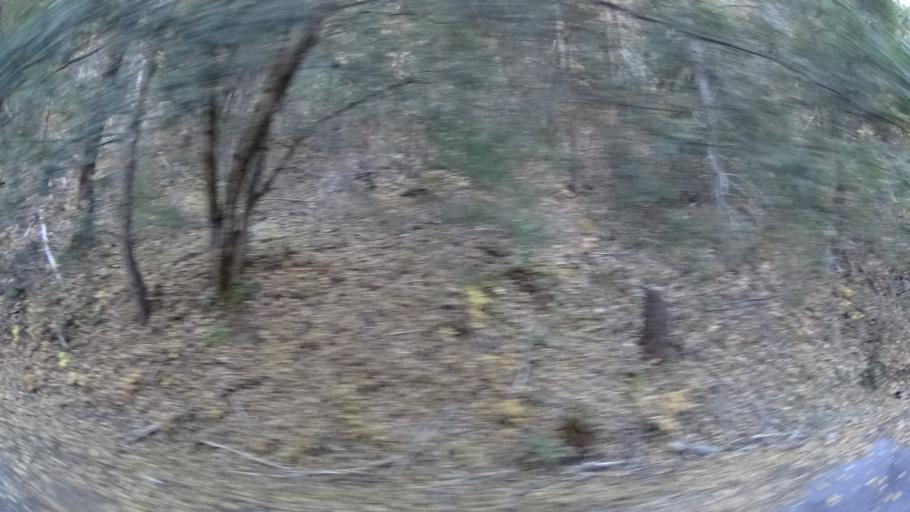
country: US
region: California
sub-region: Siskiyou County
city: Yreka
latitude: 41.8427
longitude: -122.9106
